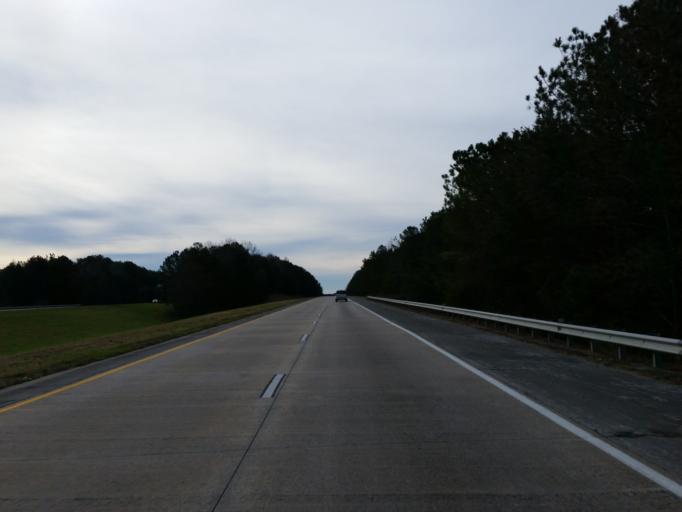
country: US
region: Georgia
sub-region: Pickens County
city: Nelson
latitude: 34.3669
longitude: -84.3916
